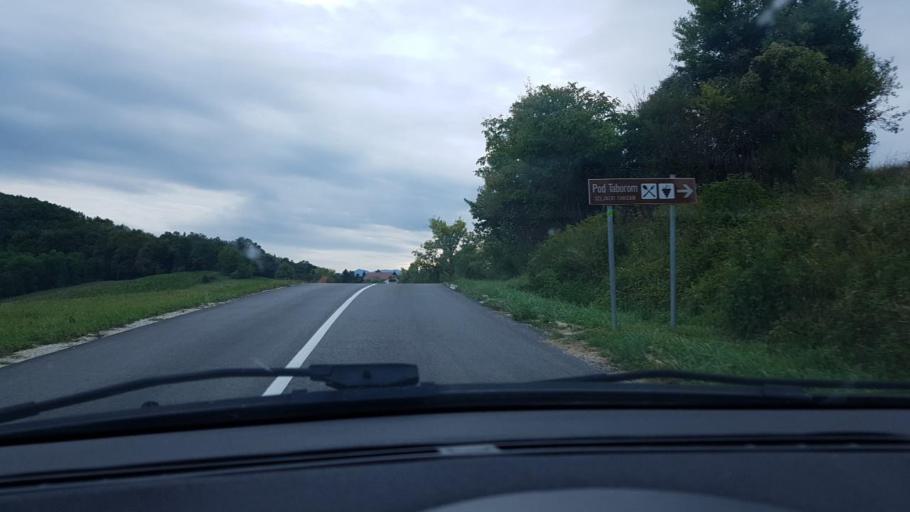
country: SI
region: Podcetrtek
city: Podcetrtek
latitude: 46.1516
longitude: 15.6485
